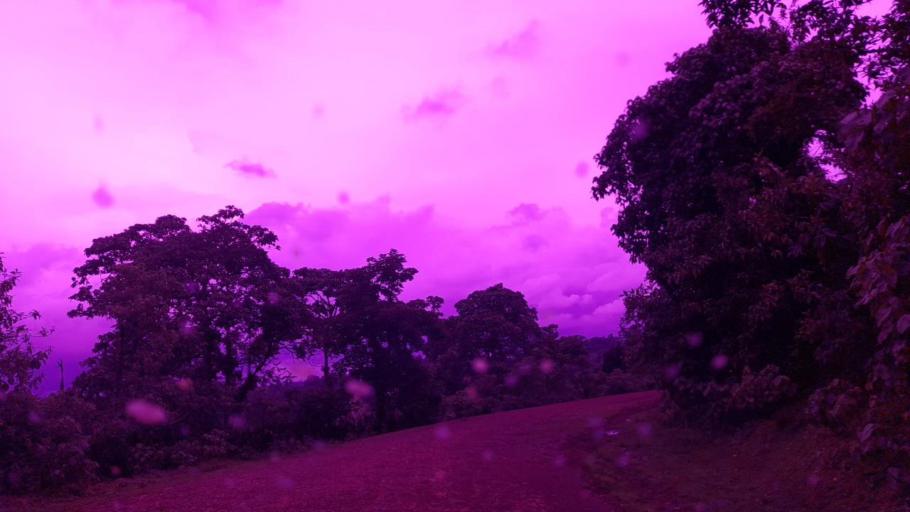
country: ET
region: Southern Nations, Nationalities, and People's Region
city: Tippi
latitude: 7.5796
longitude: 35.6665
